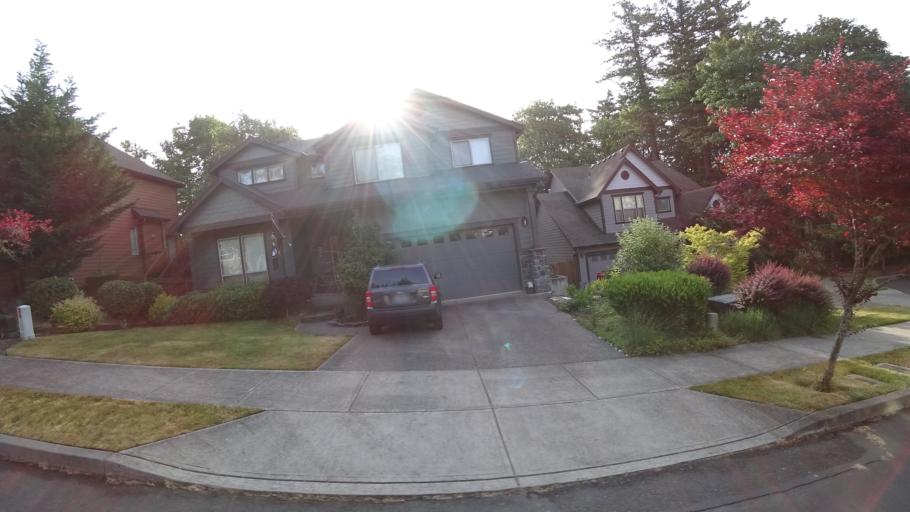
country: US
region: Oregon
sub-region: Clackamas County
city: Happy Valley
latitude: 45.4624
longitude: -122.5142
